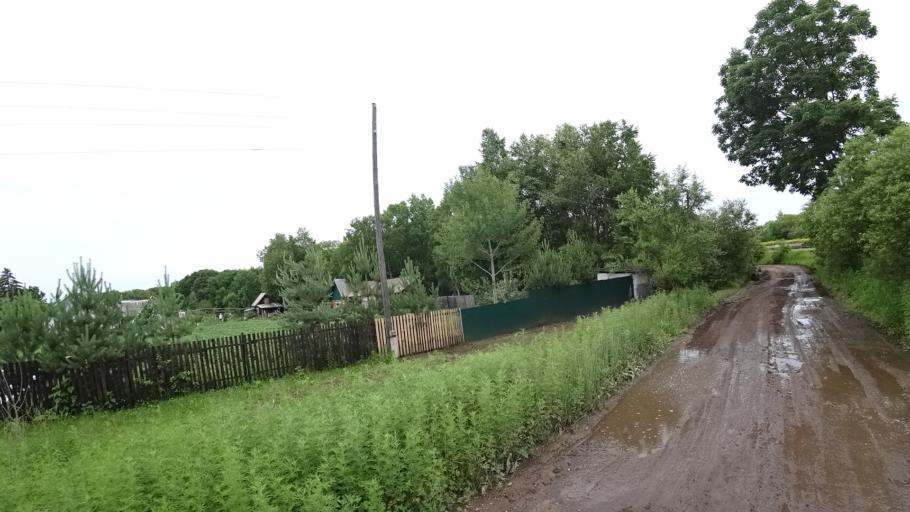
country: RU
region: Primorskiy
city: Novosysoyevka
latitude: 44.2072
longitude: 133.3432
